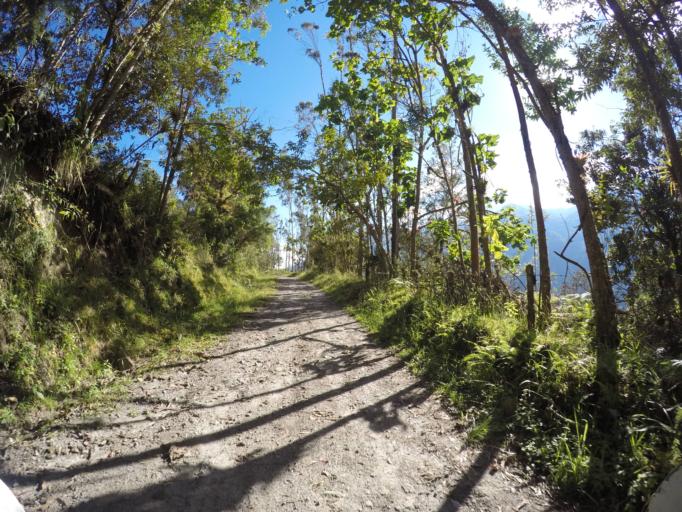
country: CO
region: Tolima
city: Cajamarca
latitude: 4.4960
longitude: -75.3971
